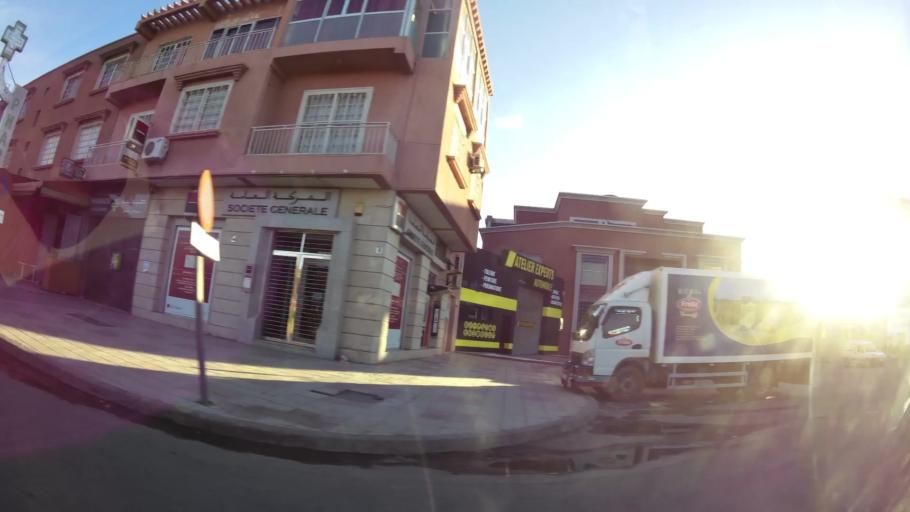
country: MA
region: Marrakech-Tensift-Al Haouz
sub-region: Marrakech
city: Marrakesh
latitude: 31.6690
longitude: -8.0393
